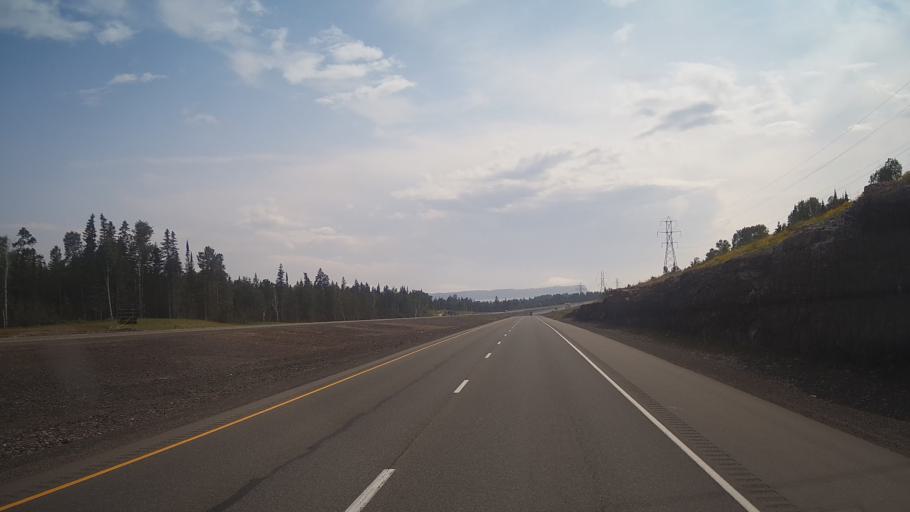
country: CA
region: Ontario
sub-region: Thunder Bay District
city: Thunder Bay
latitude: 48.5889
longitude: -88.7955
